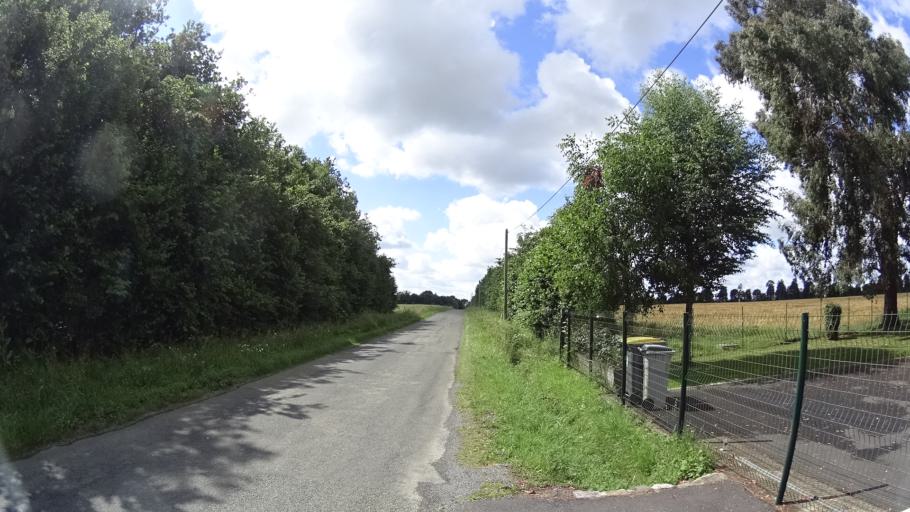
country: FR
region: Brittany
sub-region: Departement d'Ille-et-Vilaine
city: Le Rheu
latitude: 48.1131
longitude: -1.8146
